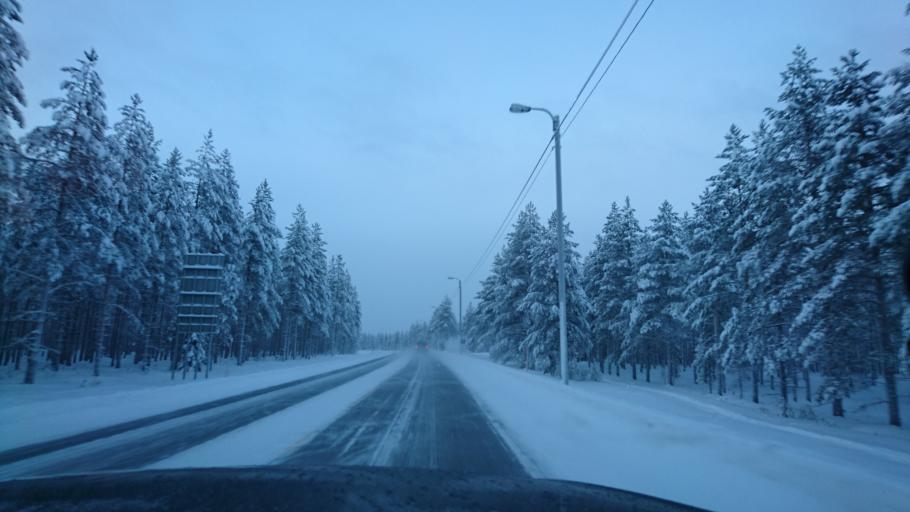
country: FI
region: Kainuu
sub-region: Kehys-Kainuu
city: Puolanka
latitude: 65.4299
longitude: 27.5293
